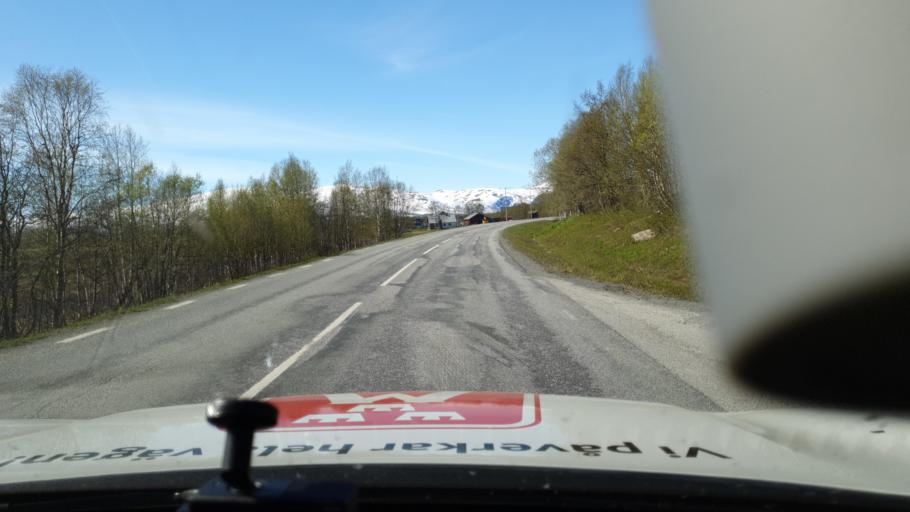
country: NO
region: Nordland
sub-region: Rana
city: Mo i Rana
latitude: 65.8054
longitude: 15.0906
